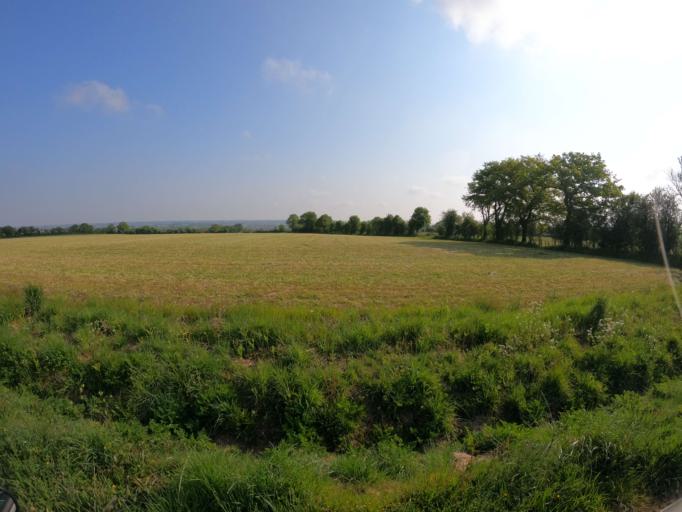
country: FR
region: Pays de la Loire
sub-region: Departement de Maine-et-Loire
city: La Romagne
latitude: 47.0650
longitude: -1.0429
